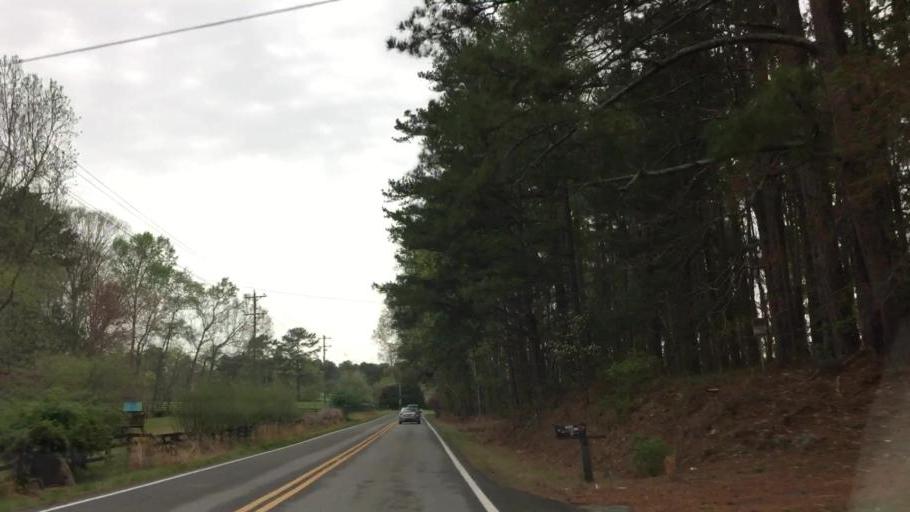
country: US
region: Georgia
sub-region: Fulton County
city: Milton
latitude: 34.1819
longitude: -84.3399
